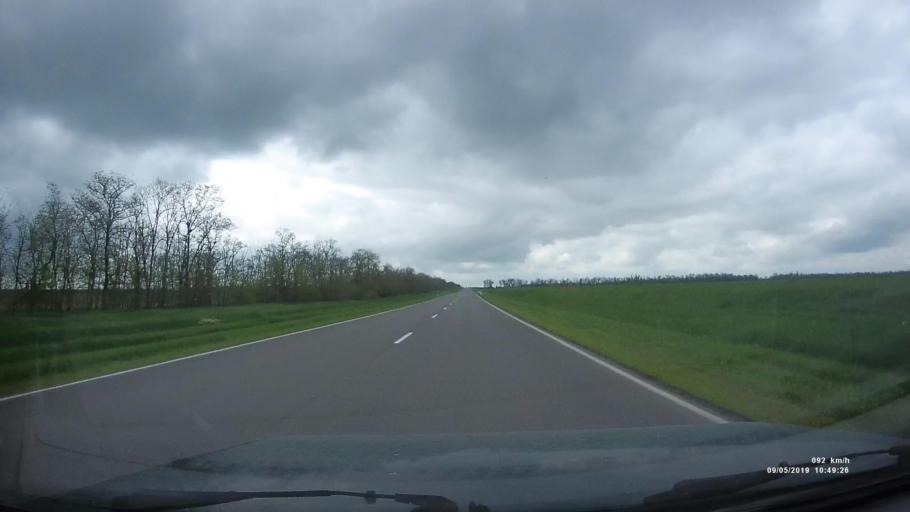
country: RU
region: Rostov
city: Peshkovo
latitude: 46.9426
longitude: 39.3567
